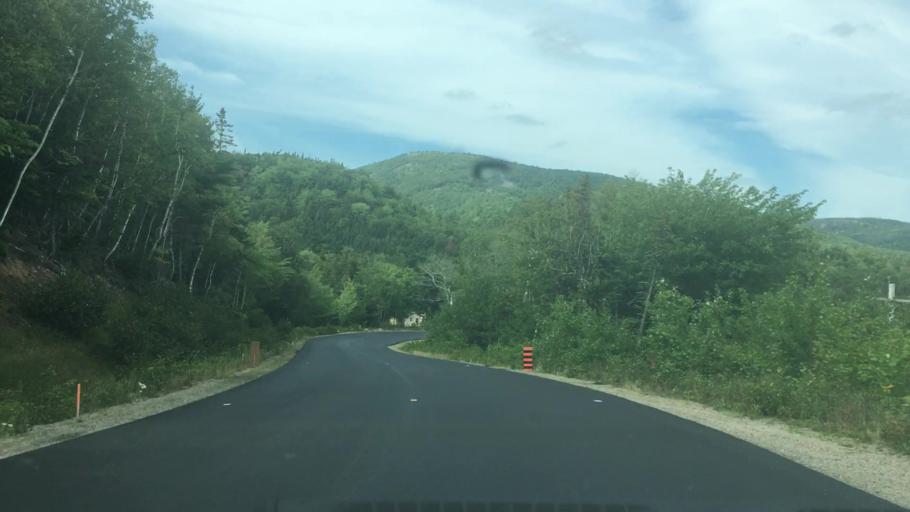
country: CA
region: Nova Scotia
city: Sydney Mines
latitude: 46.5431
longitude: -60.4146
